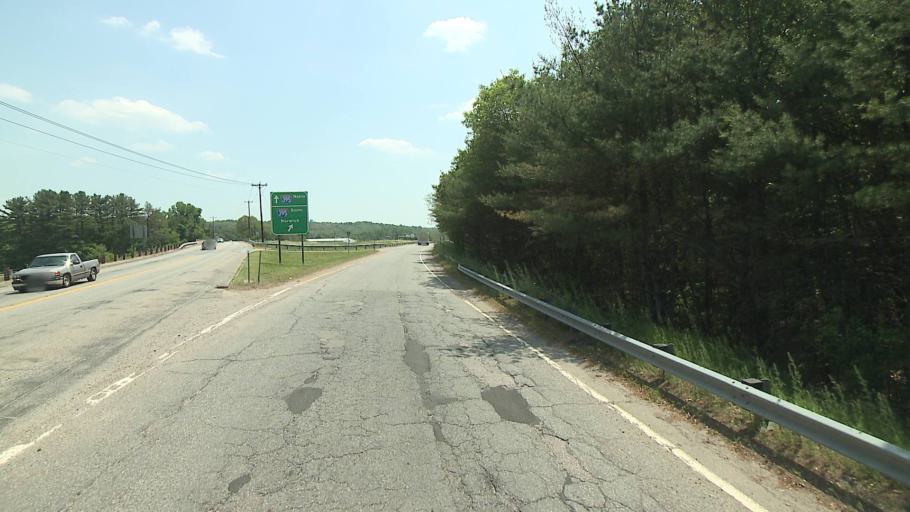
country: US
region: Connecticut
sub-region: Windham County
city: Putnam
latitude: 41.9005
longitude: -71.9008
